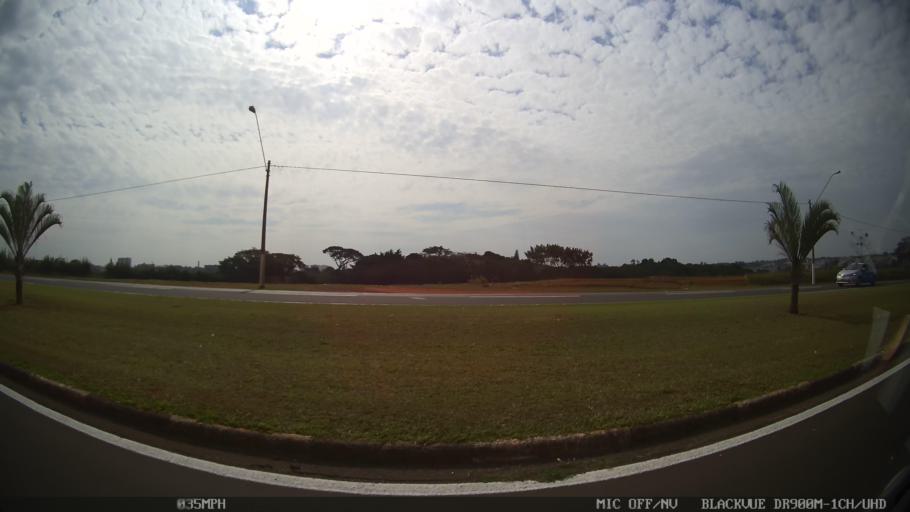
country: BR
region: Sao Paulo
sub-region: Paulinia
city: Paulinia
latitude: -22.7944
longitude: -47.1491
